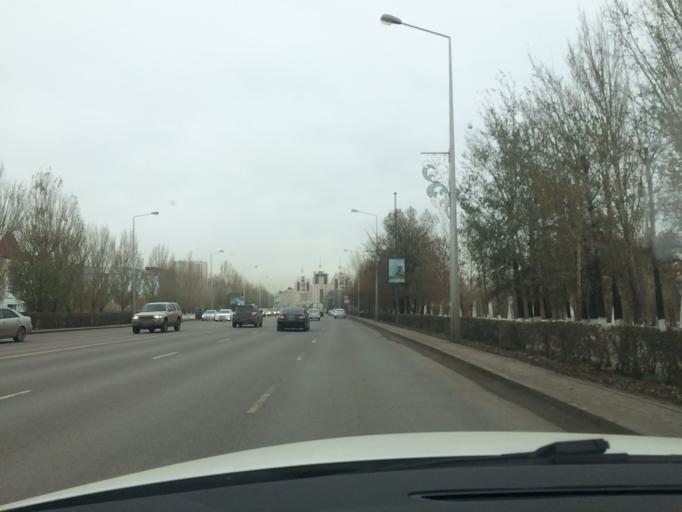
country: KZ
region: Astana Qalasy
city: Astana
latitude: 51.1490
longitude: 71.4127
